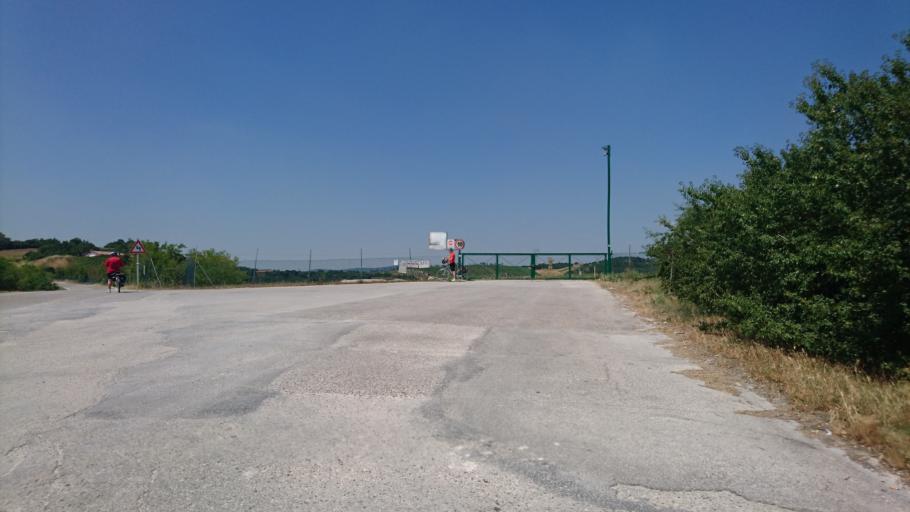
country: IT
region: Veneto
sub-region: Provincia di Vicenza
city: Albettone
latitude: 45.3696
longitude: 11.6011
